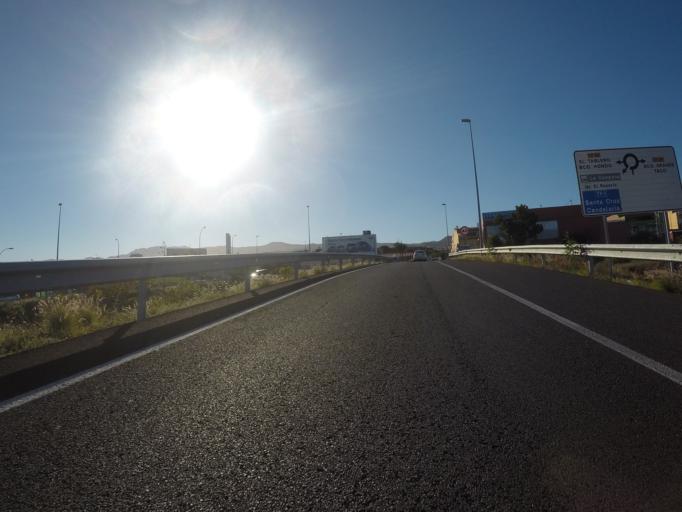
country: ES
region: Canary Islands
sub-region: Provincia de Santa Cruz de Tenerife
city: La Laguna
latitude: 28.4201
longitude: -16.3196
